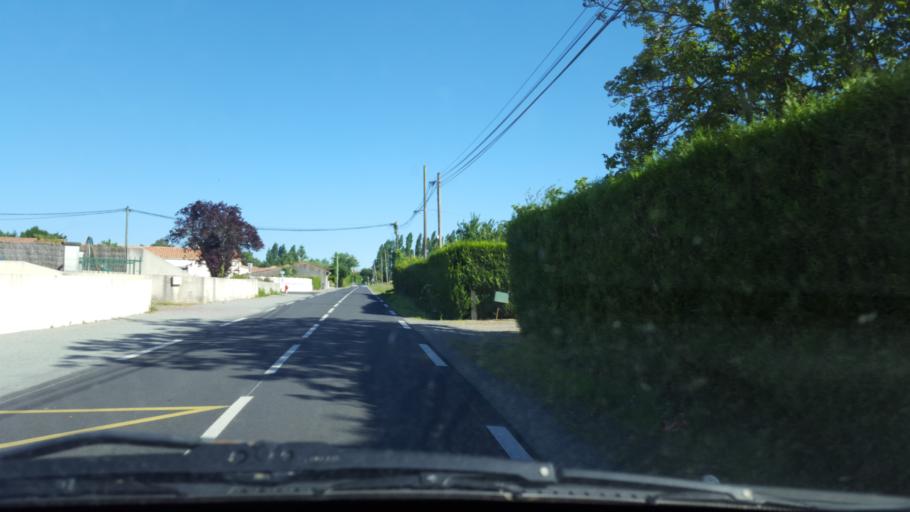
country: FR
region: Pays de la Loire
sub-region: Departement de la Loire-Atlantique
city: Saint-Philbert-de-Grand-Lieu
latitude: 47.0324
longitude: -1.6806
